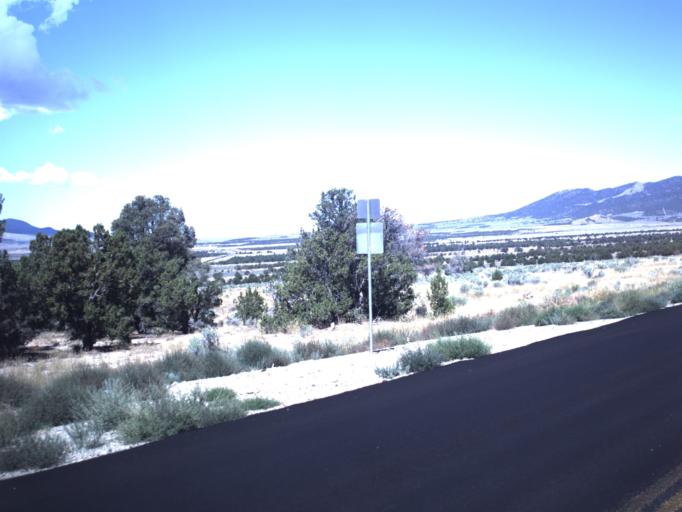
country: US
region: Utah
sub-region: Juab County
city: Mona
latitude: 39.9212
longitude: -112.1451
